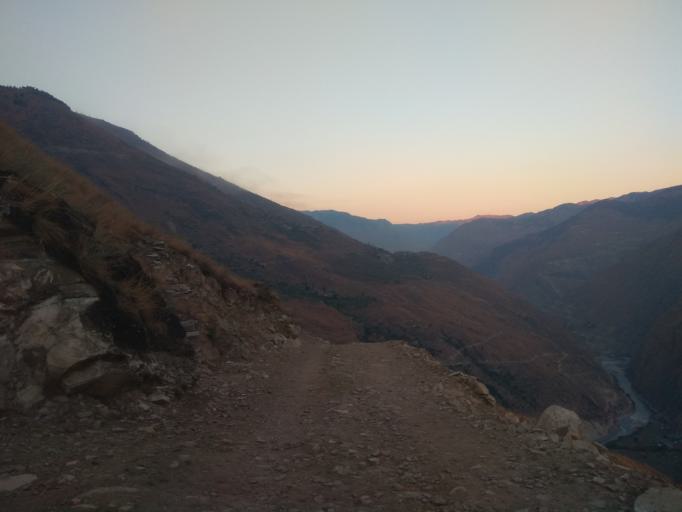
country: NP
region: Mid Western
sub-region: Bheri Zone
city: Dailekh
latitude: 29.2663
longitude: 81.6924
